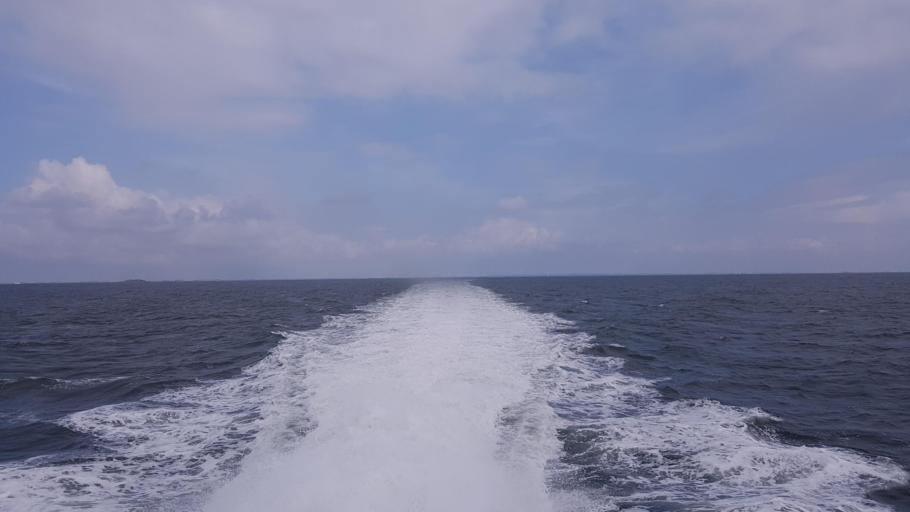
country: DE
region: Schleswig-Holstein
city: Grode
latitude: 54.6084
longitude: 8.6803
